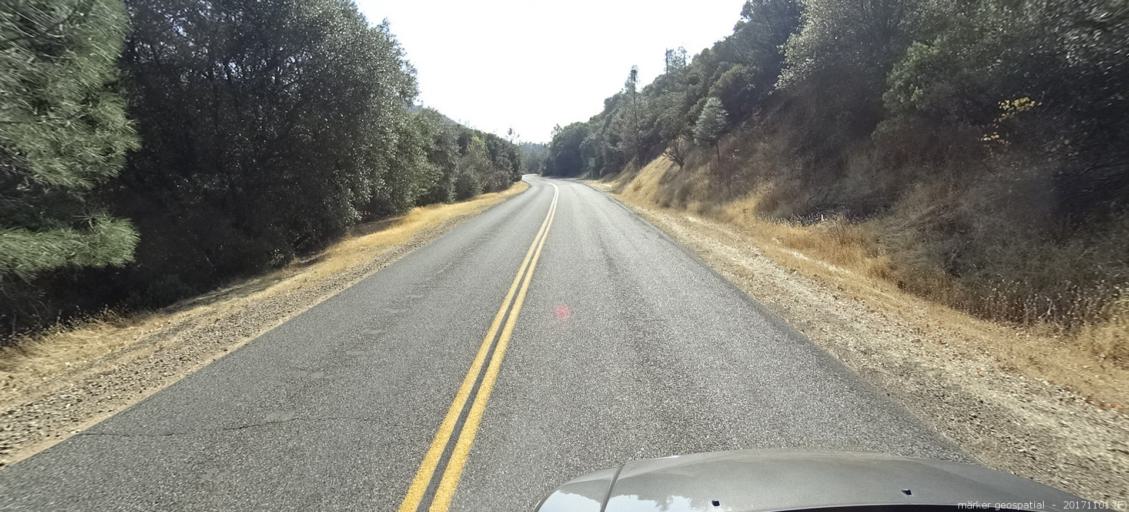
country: US
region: California
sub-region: Shasta County
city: Central Valley (historical)
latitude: 40.7102
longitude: -122.4057
